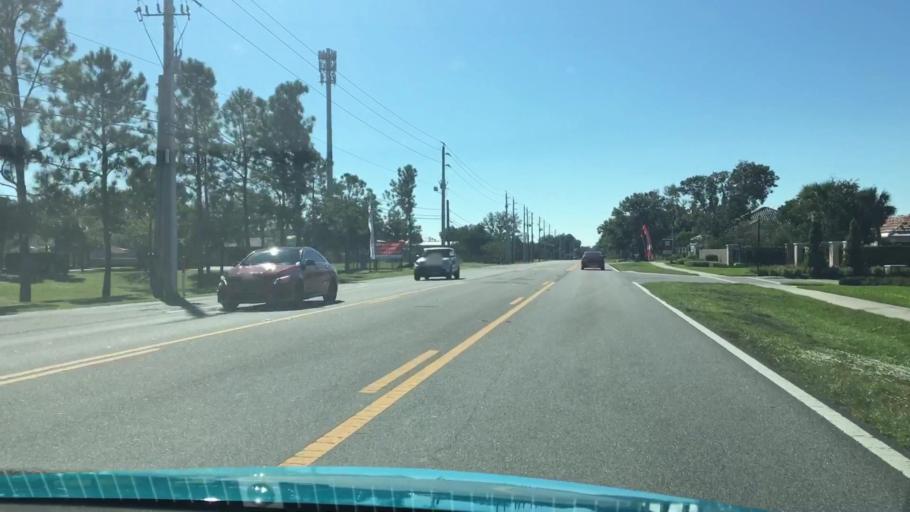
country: US
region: Florida
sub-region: Seminole County
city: Heathrow
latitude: 28.7992
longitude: -81.3630
